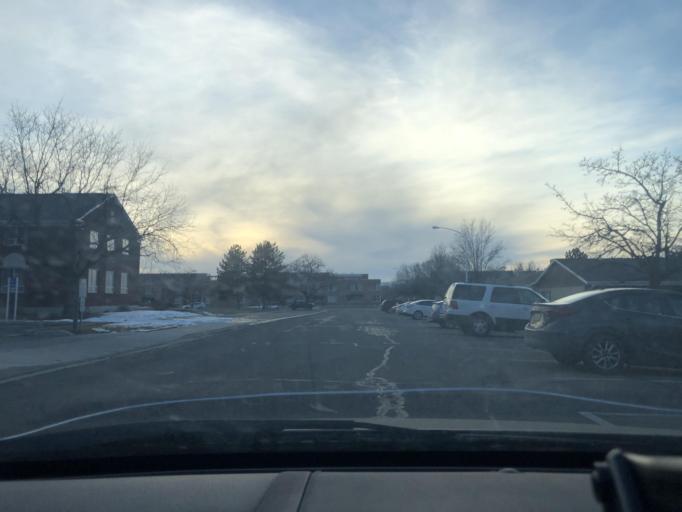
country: US
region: Utah
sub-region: Utah County
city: Provo
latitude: 40.2326
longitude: -111.6416
